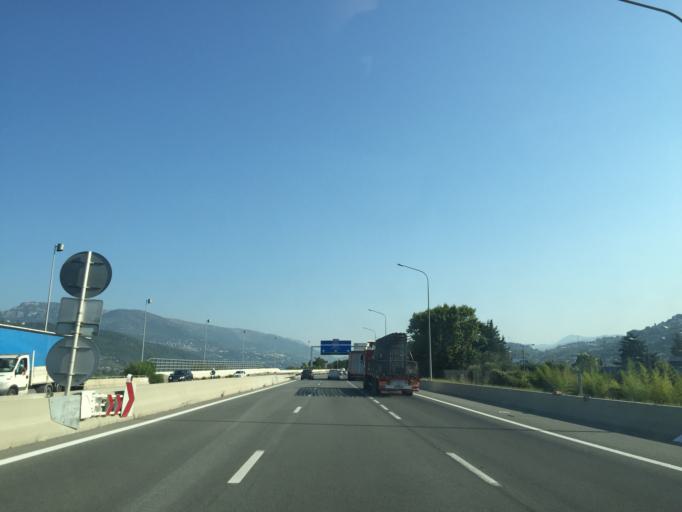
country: FR
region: Provence-Alpes-Cote d'Azur
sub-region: Departement des Alpes-Maritimes
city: Saint-Laurent-du-Var
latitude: 43.7022
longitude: 7.1884
